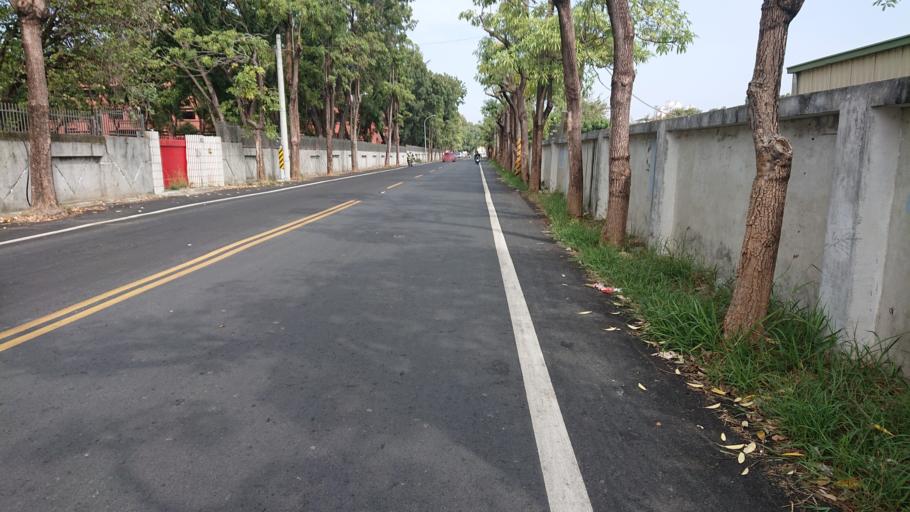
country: TW
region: Taiwan
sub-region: Tainan
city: Tainan
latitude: 23.0203
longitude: 120.2550
